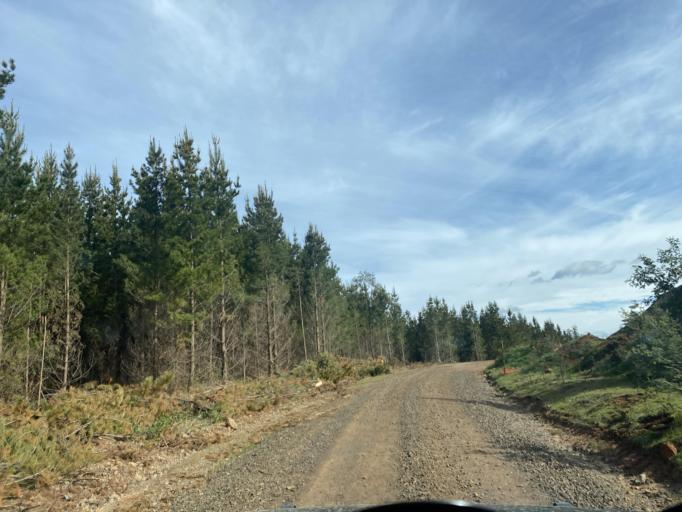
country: AU
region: Victoria
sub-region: Mansfield
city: Mansfield
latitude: -36.8327
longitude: 146.1797
